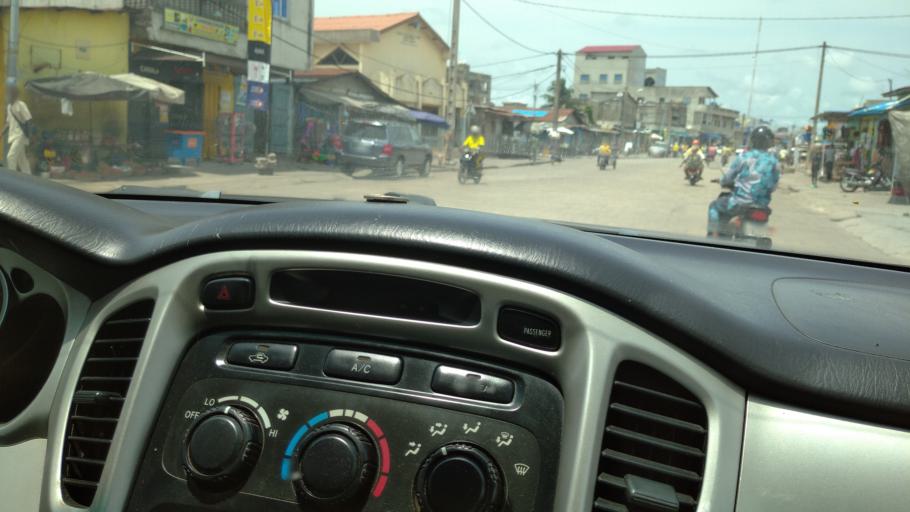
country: BJ
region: Littoral
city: Cotonou
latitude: 6.3929
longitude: 2.4471
